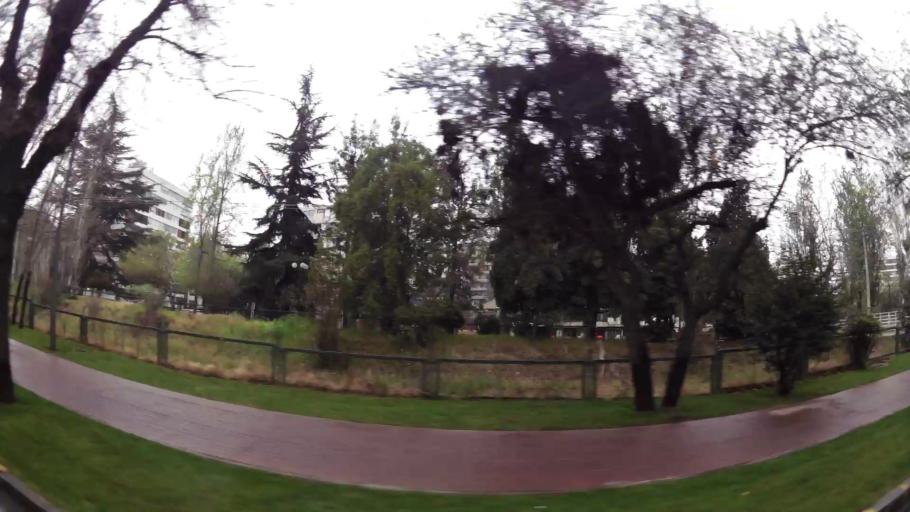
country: CL
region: Santiago Metropolitan
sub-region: Provincia de Santiago
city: Villa Presidente Frei, Nunoa, Santiago, Chile
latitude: -33.4240
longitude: -70.5934
